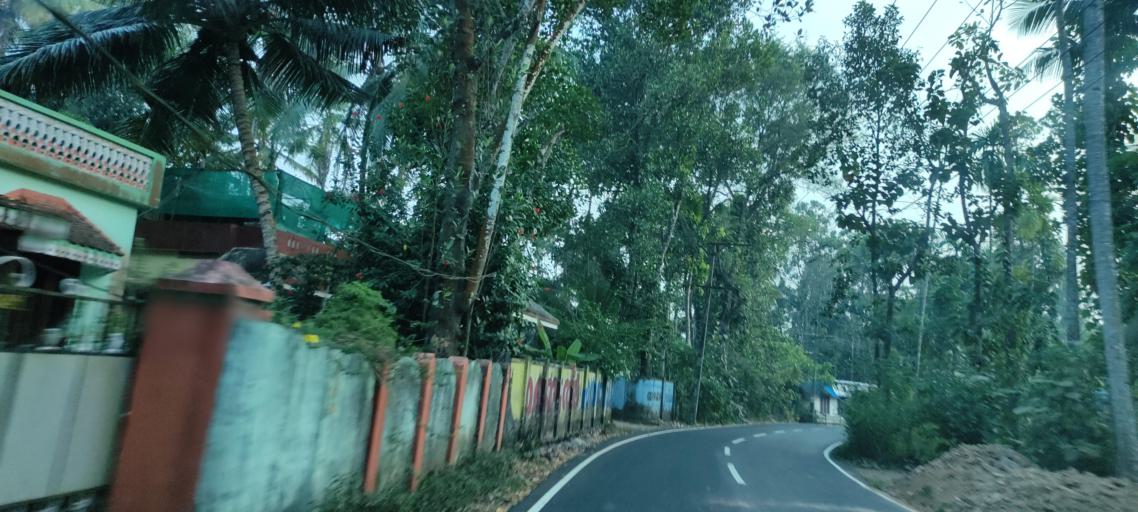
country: IN
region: Kerala
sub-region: Alappuzha
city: Mavelikara
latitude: 9.2711
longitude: 76.5522
